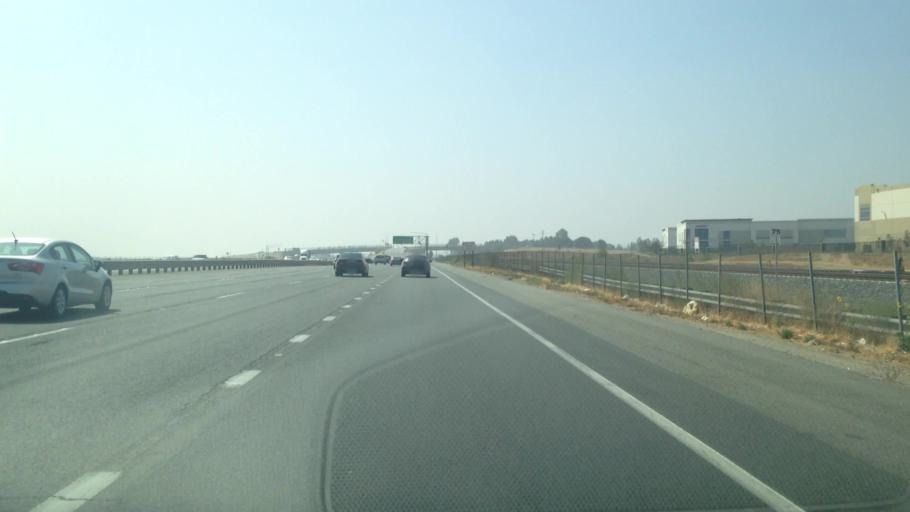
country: US
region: California
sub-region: Riverside County
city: March Air Force Base
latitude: 33.8949
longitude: -117.2739
